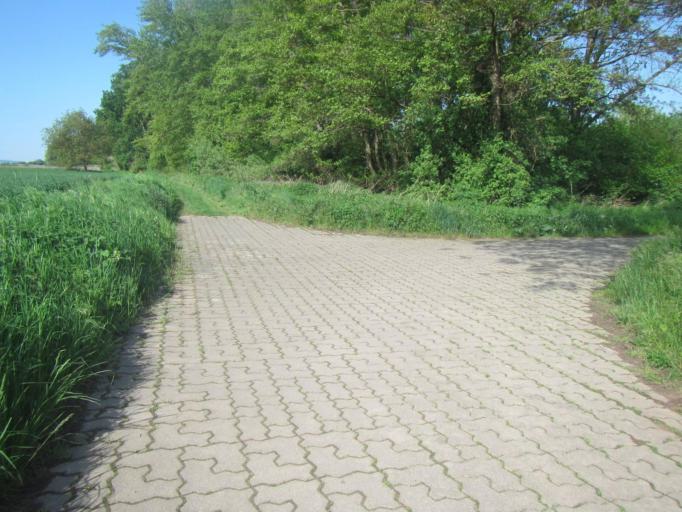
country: DE
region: Rheinland-Pfalz
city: Kleinfischlingen
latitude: 49.2566
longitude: 8.1895
